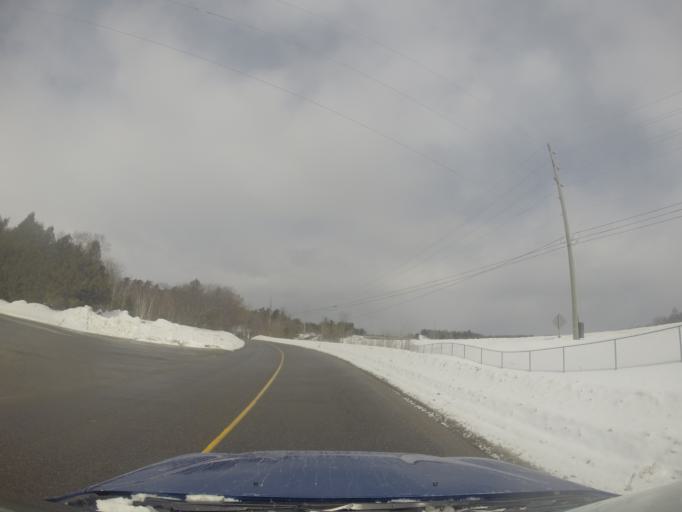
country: CA
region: Ontario
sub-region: Parry Sound District
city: Parry Sound
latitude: 45.3652
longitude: -80.0242
